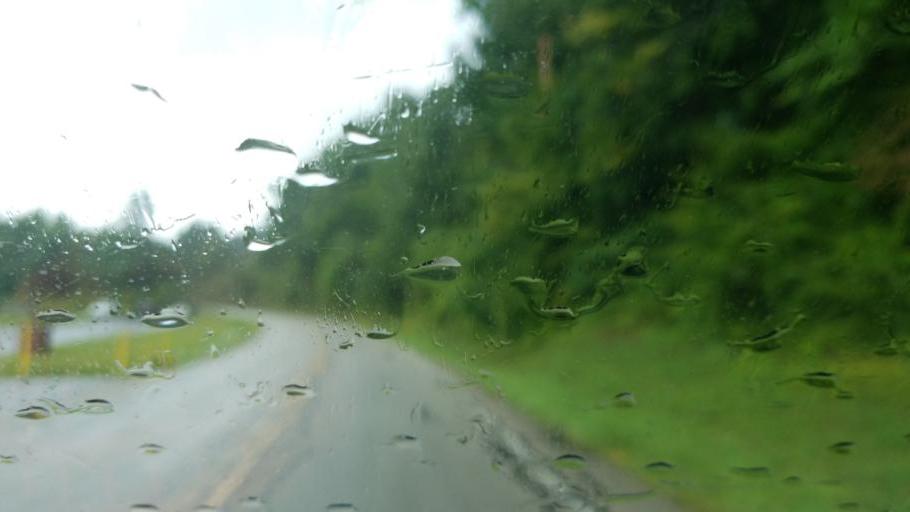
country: US
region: Kentucky
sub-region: Rowan County
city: Morehead
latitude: 38.1660
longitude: -83.4453
